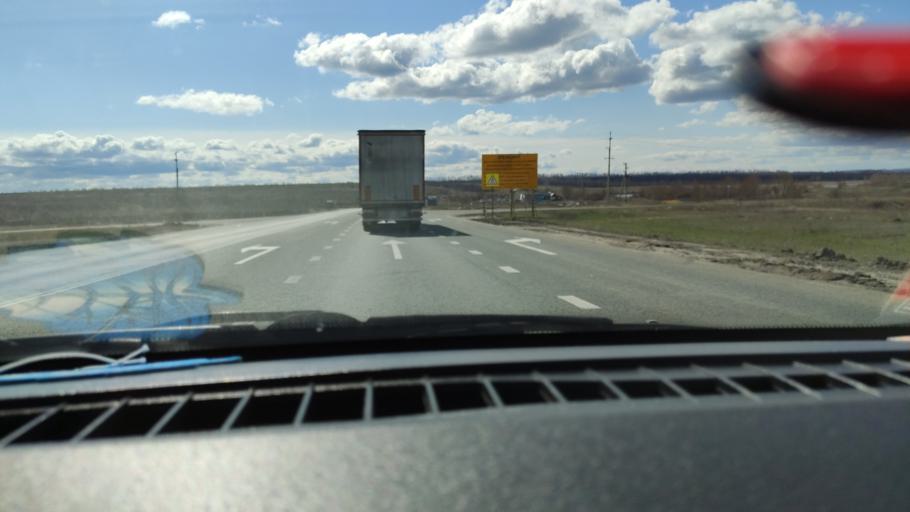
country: RU
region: Saratov
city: Dukhovnitskoye
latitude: 52.7413
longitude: 48.2538
